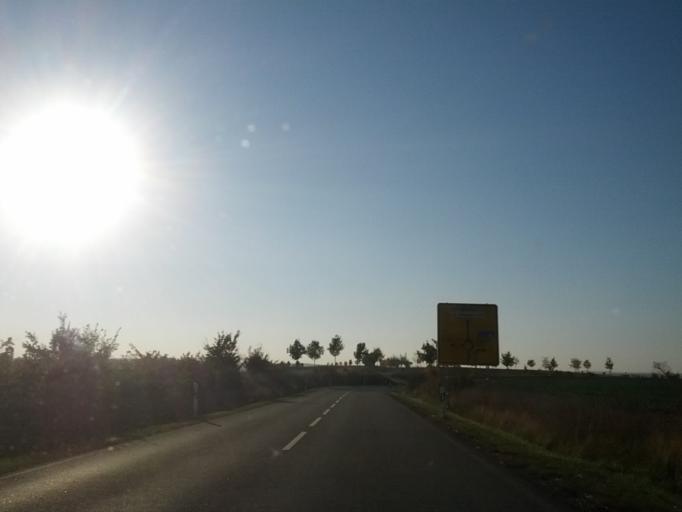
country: DE
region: Thuringia
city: Schwaara
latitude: 50.8964
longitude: 12.1233
